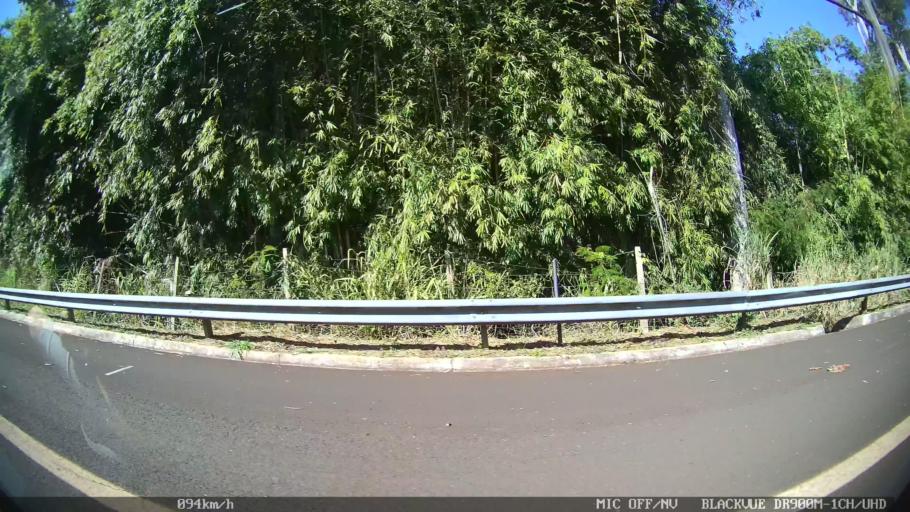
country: BR
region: Sao Paulo
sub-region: Batatais
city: Batatais
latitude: -20.7307
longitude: -47.5231
